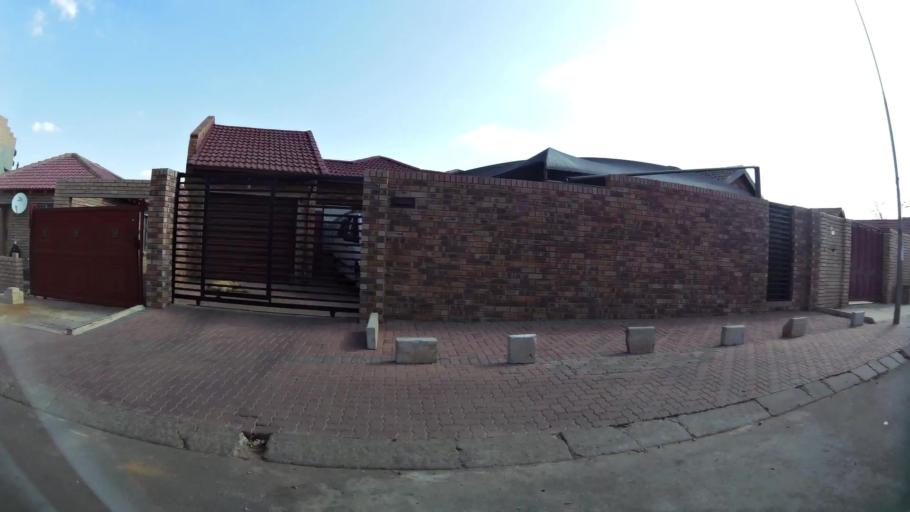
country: ZA
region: Gauteng
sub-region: City of Johannesburg Metropolitan Municipality
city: Soweto
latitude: -26.2642
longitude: 27.8855
